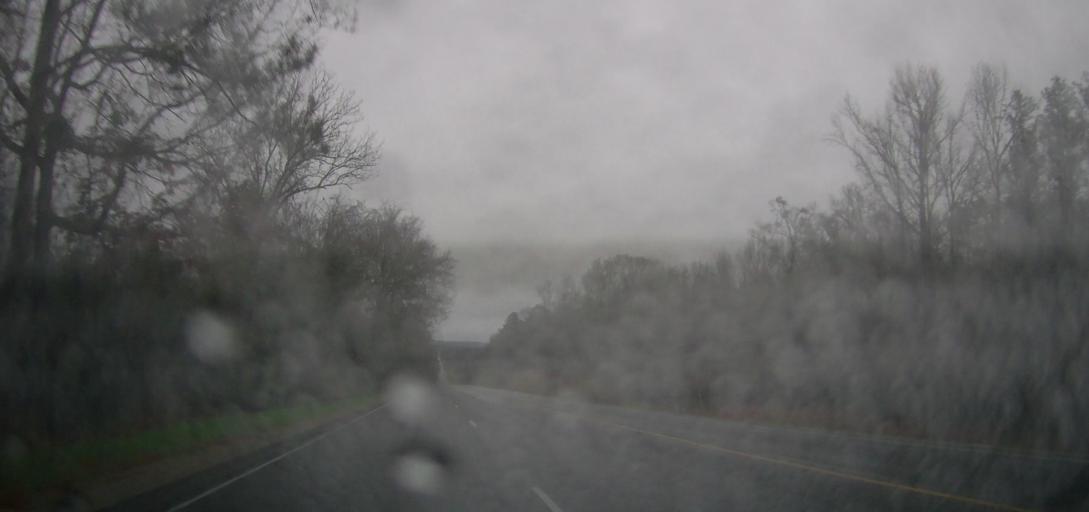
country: US
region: Alabama
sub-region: Autauga County
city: Pine Level
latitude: 32.5791
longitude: -86.6883
